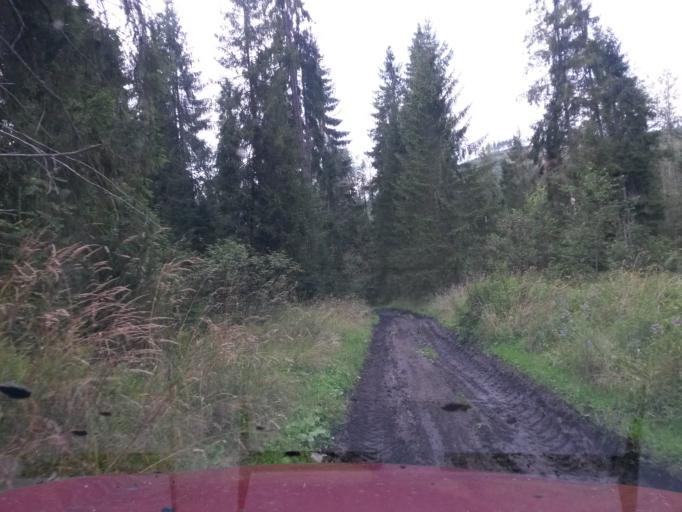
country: PL
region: Lesser Poland Voivodeship
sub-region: Powiat tatrzanski
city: Bukowina Tatrzanska
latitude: 49.2922
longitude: 20.1718
